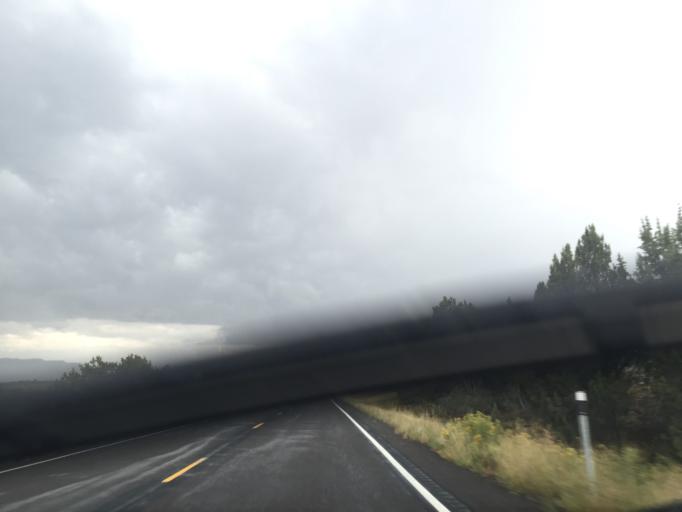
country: US
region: Utah
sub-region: Kane County
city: Kanab
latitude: 37.2427
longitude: -112.7525
